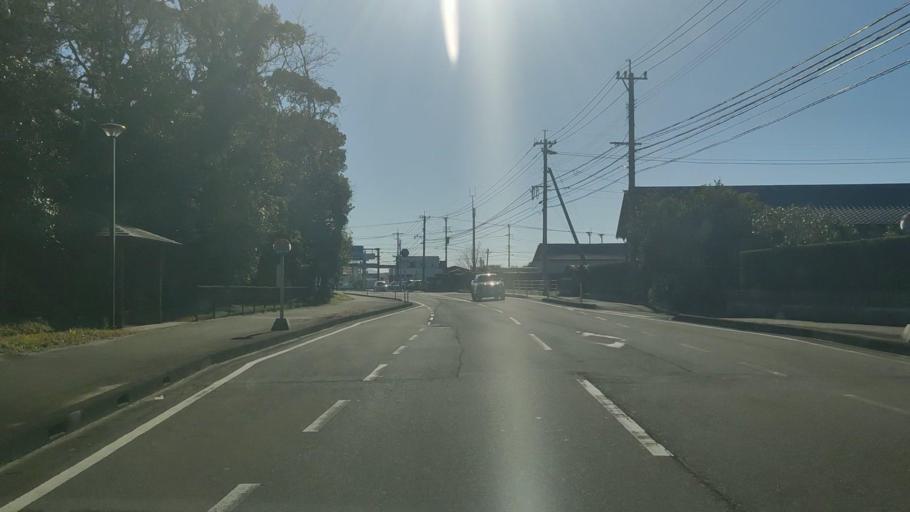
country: JP
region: Miyazaki
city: Miyazaki-shi
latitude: 31.9577
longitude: 131.4634
